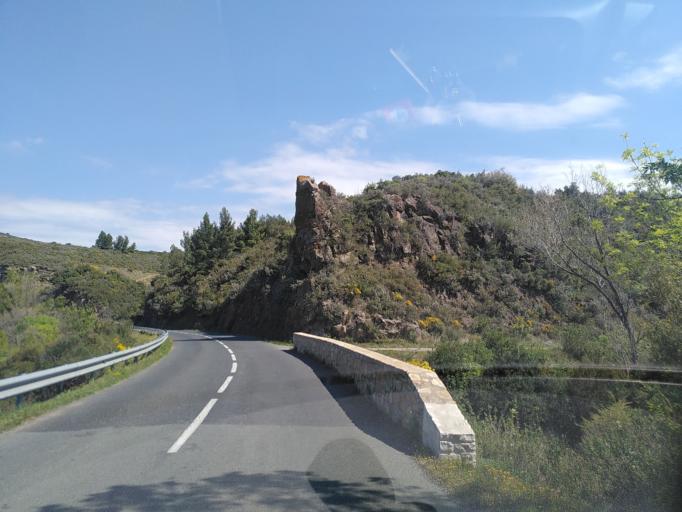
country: FR
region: Languedoc-Roussillon
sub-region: Departement de l'Aude
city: Portel-des-Corbieres
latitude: 42.9885
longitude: 2.7889
